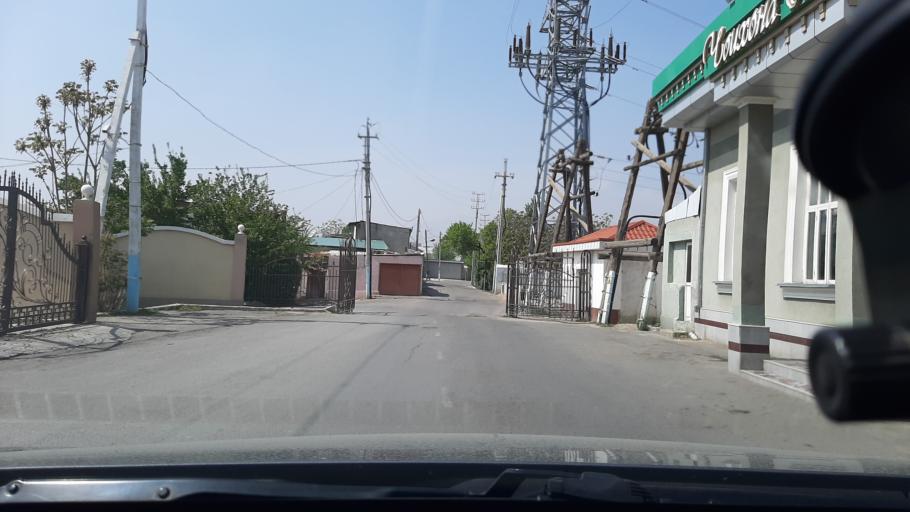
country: TJ
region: Viloyati Sughd
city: Khujand
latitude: 40.2884
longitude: 69.6129
